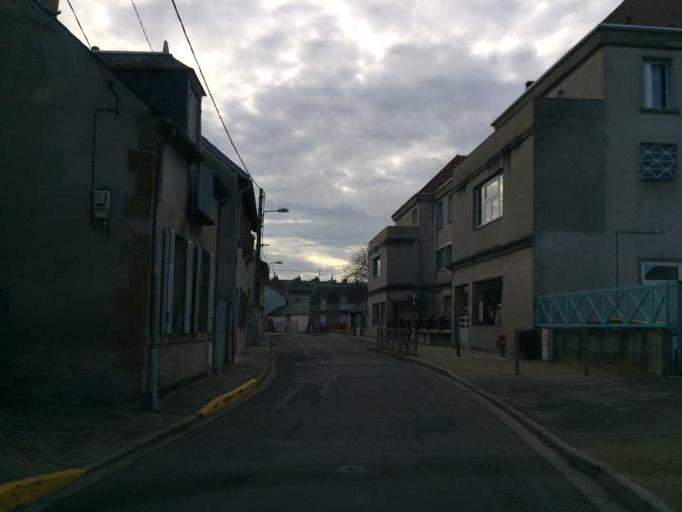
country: FR
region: Auvergne
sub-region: Departement de l'Allier
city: Moulins
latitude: 46.5708
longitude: 3.3371
